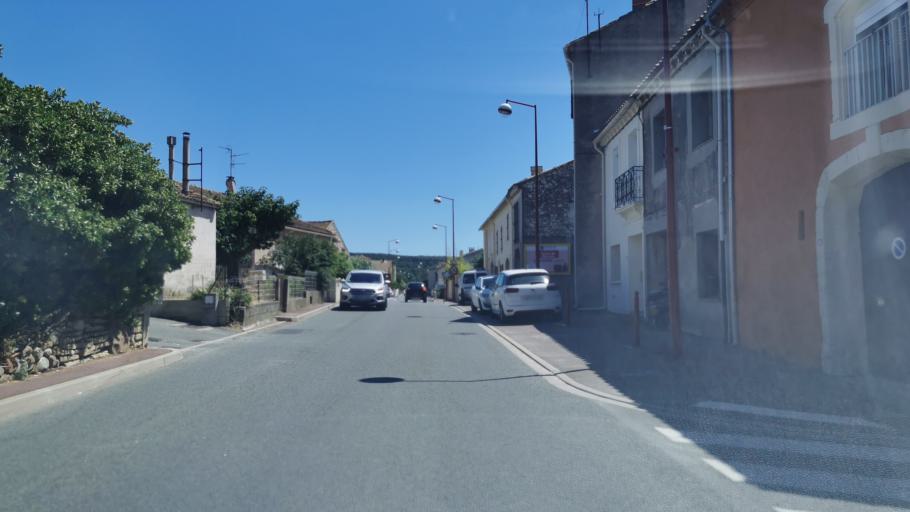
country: FR
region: Languedoc-Roussillon
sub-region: Departement de l'Aude
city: Vinassan
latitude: 43.2009
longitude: 3.0745
